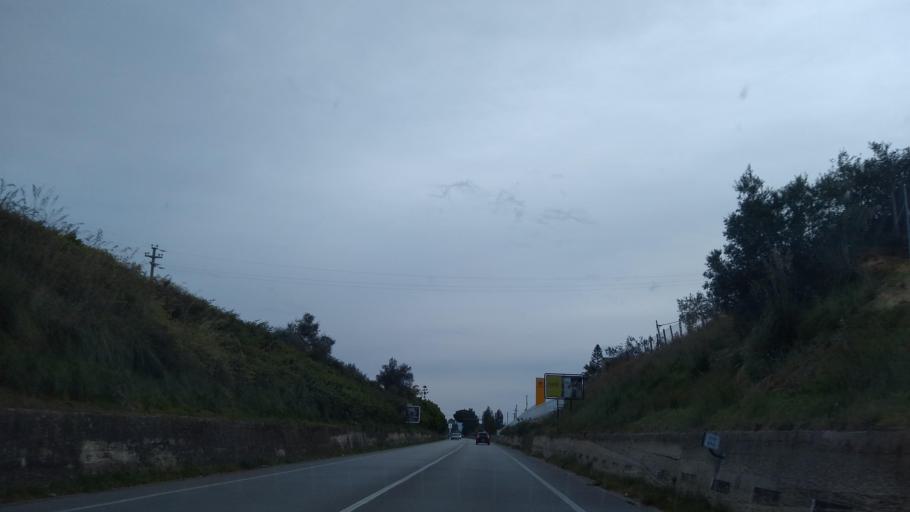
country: IT
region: Sicily
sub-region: Palermo
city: Partinico
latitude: 38.0343
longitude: 13.0990
